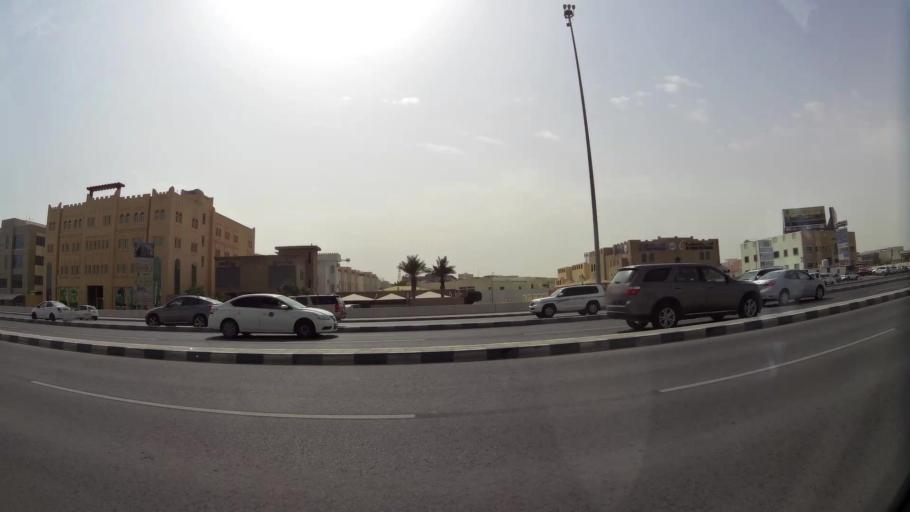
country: QA
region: Baladiyat ad Dawhah
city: Doha
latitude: 25.2770
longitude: 51.4908
